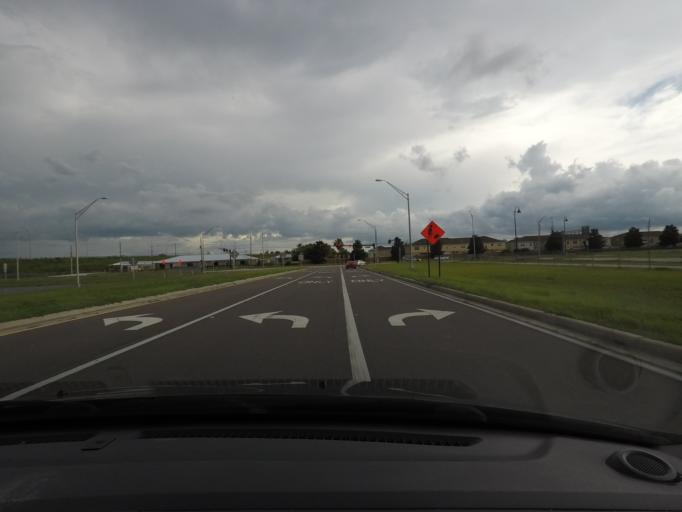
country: US
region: Florida
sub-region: Orange County
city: Conway
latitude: 28.4155
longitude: -81.2294
